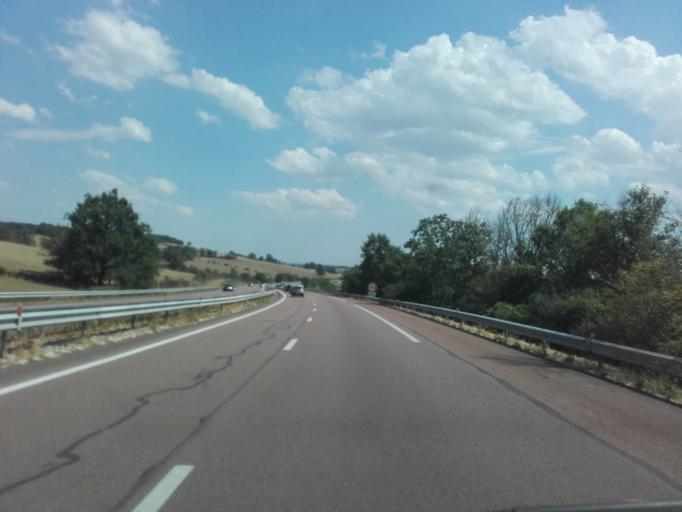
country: FR
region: Bourgogne
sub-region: Departement de l'Yonne
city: Avallon
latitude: 47.5519
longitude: 3.9564
